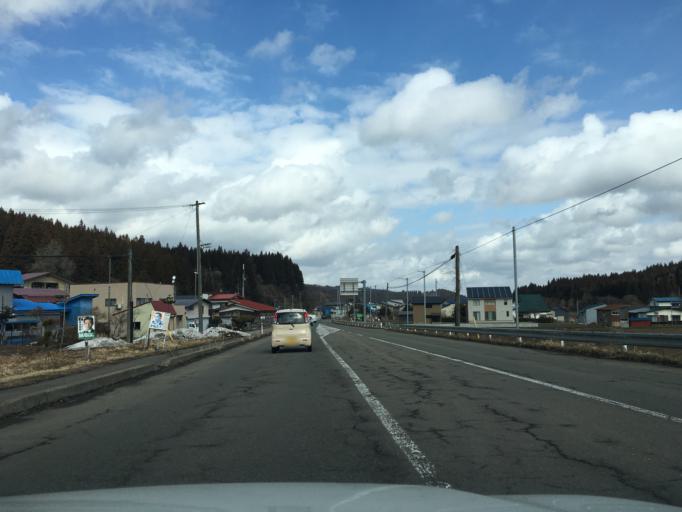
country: JP
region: Akita
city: Takanosu
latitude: 40.0320
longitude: 140.2747
